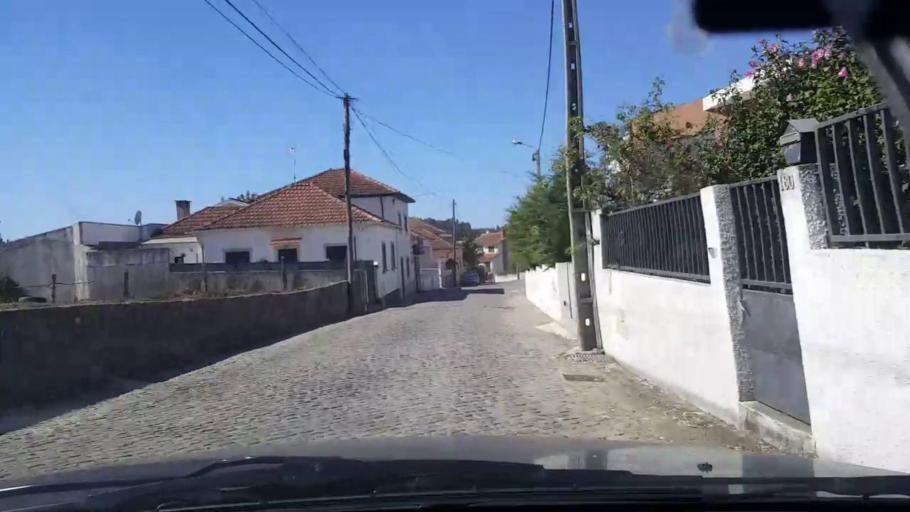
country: PT
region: Porto
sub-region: Maia
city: Gemunde
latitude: 41.2963
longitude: -8.6824
